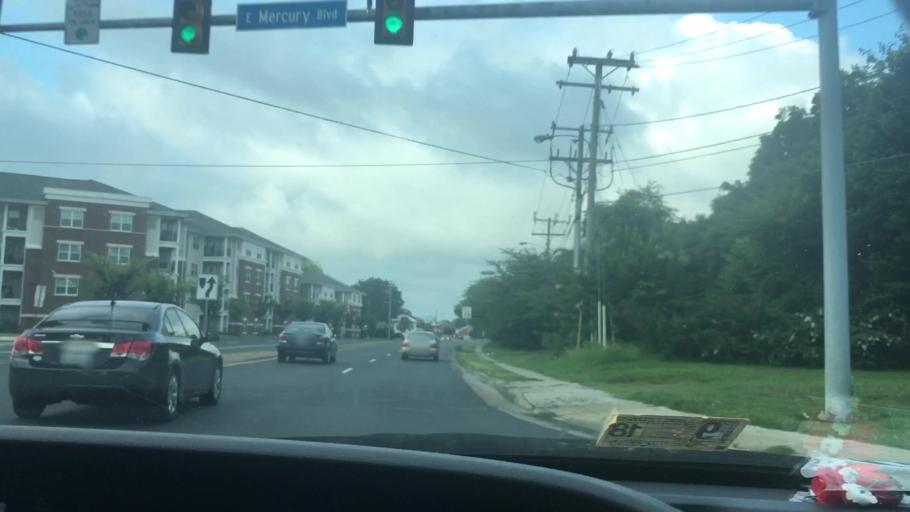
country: US
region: Virginia
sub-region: City of Hampton
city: East Hampton
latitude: 37.0270
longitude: -76.3235
